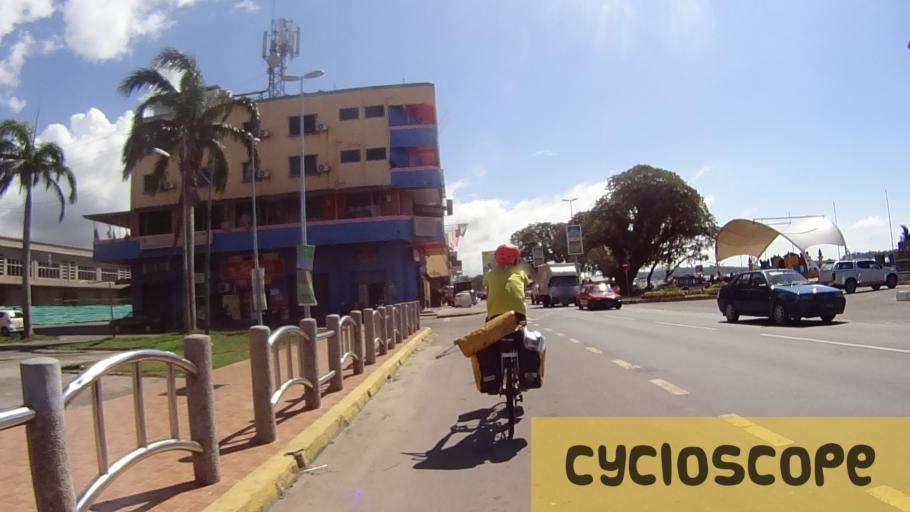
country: MY
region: Sabah
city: Beaufort
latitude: 5.0804
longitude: 115.5505
